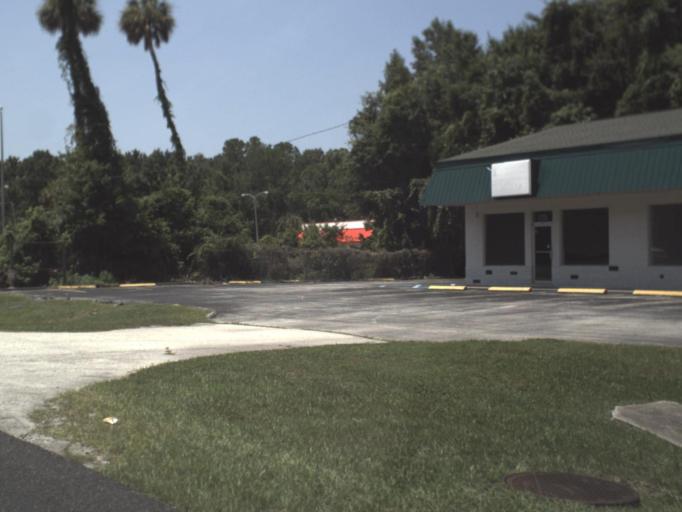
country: US
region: Florida
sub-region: Citrus County
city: Homosassa Springs
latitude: 28.8105
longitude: -82.5767
